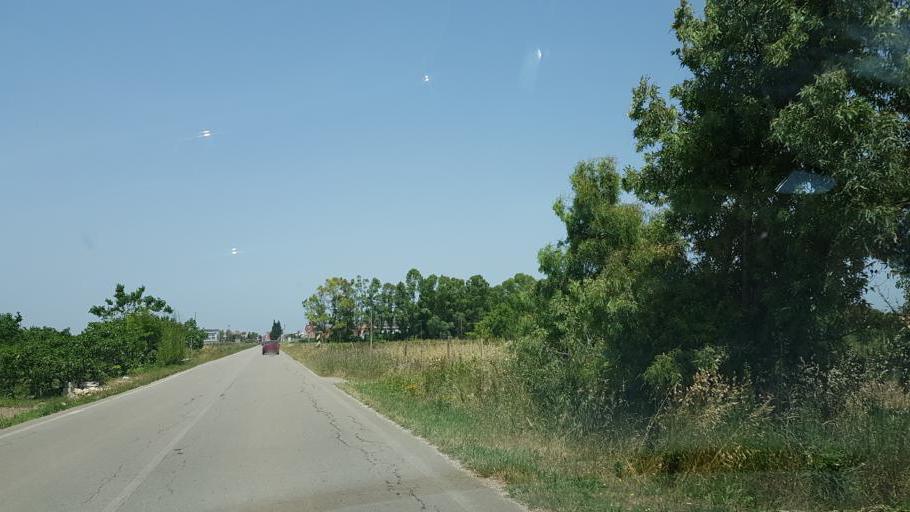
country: IT
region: Apulia
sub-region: Provincia di Brindisi
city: San Pancrazio Salentino
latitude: 40.4037
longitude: 17.8358
